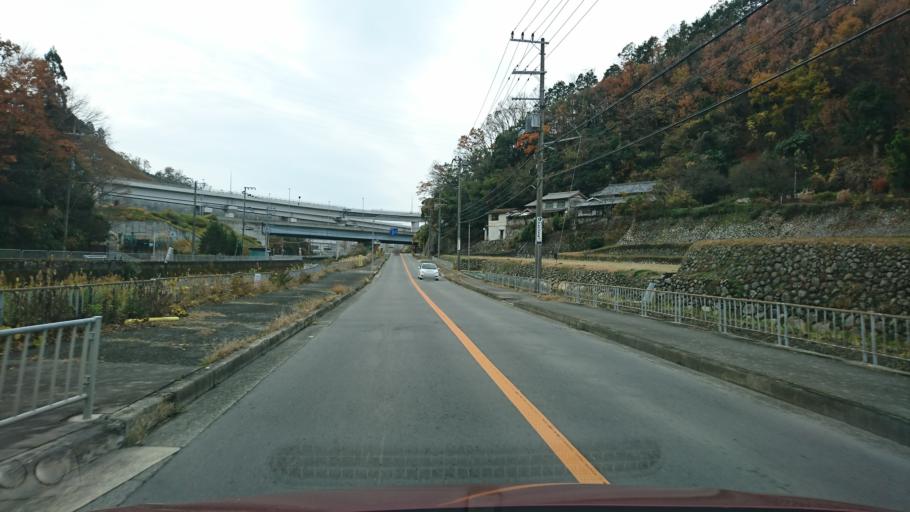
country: JP
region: Osaka
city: Mino
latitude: 34.8788
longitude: 135.4584
